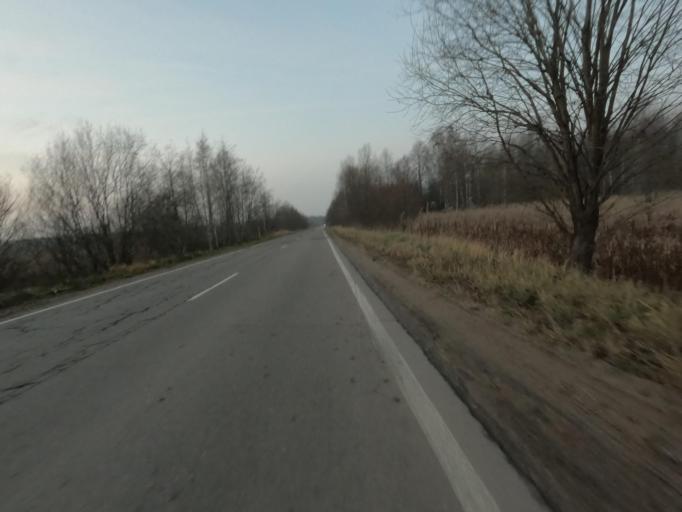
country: RU
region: Leningrad
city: Kirovsk
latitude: 59.8608
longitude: 30.9810
